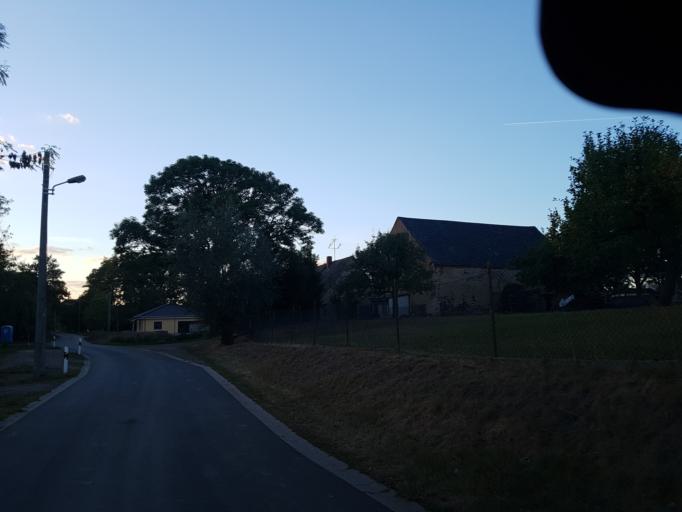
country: DE
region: Saxony
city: Oschatz
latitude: 51.2975
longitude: 13.1658
